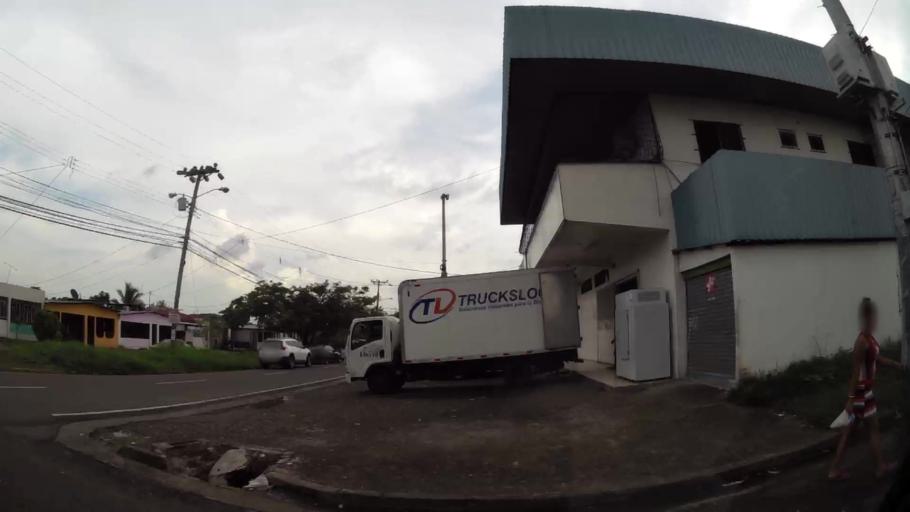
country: PA
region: Panama
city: Cabra Numero Uno
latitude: 9.0952
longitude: -79.3447
